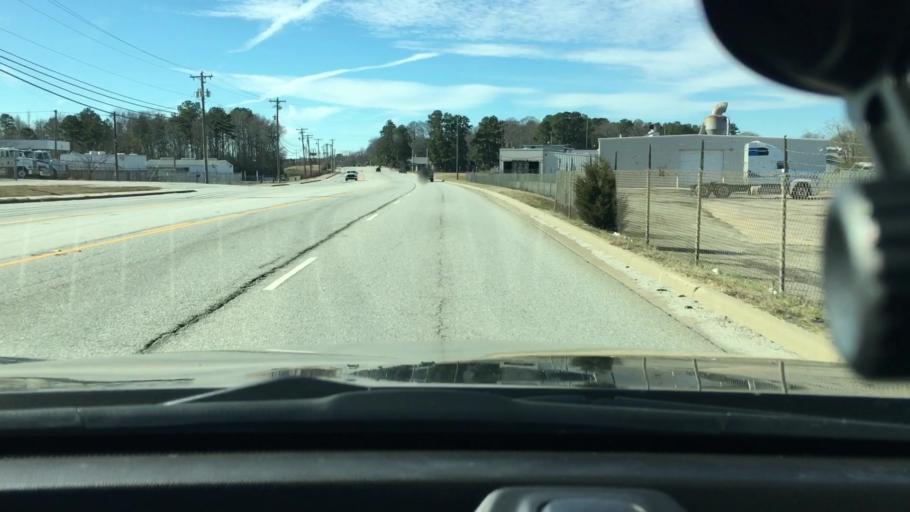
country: US
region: South Carolina
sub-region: Spartanburg County
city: Spartanburg
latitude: 34.9226
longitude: -81.8800
